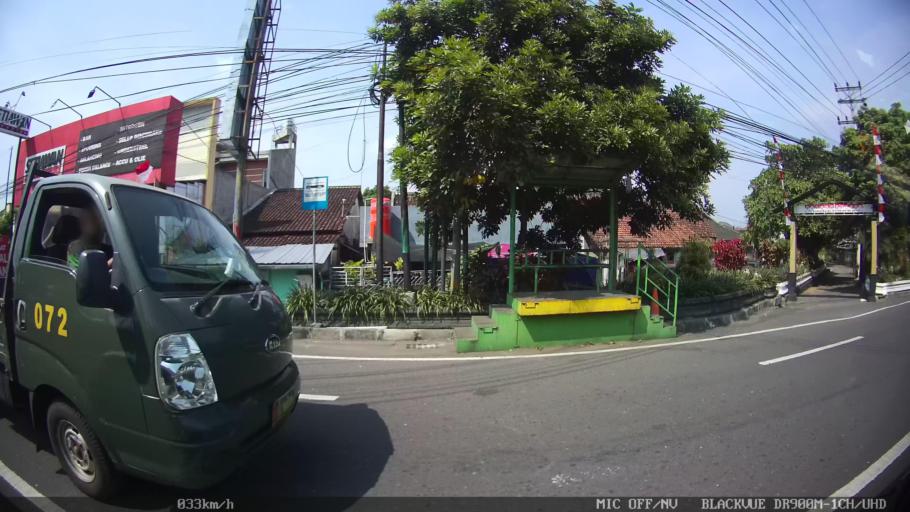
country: ID
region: Daerah Istimewa Yogyakarta
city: Yogyakarta
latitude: -7.7896
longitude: 110.3590
